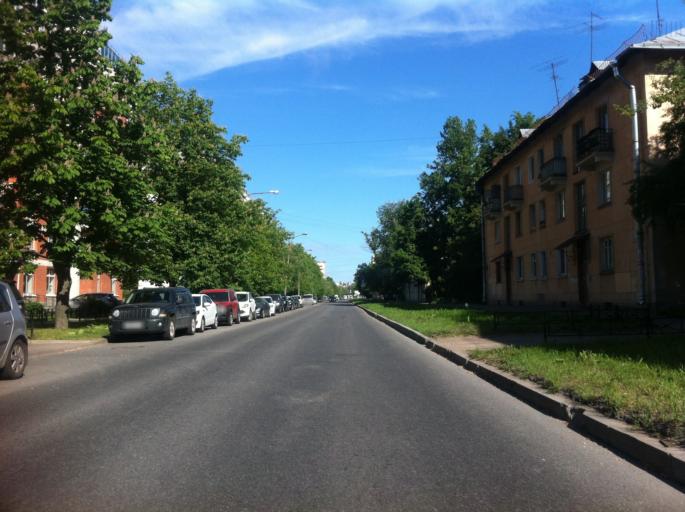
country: RU
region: St.-Petersburg
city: Dachnoye
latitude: 59.8380
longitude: 30.2513
